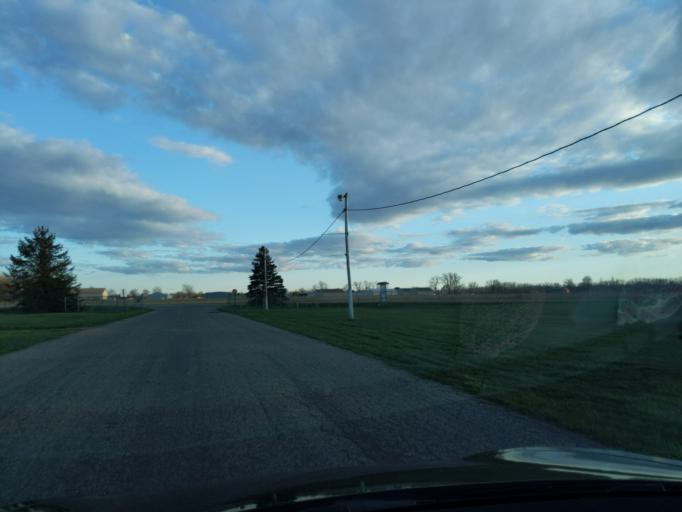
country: US
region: Michigan
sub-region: Ingham County
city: Mason
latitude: 42.5682
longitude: -84.4278
